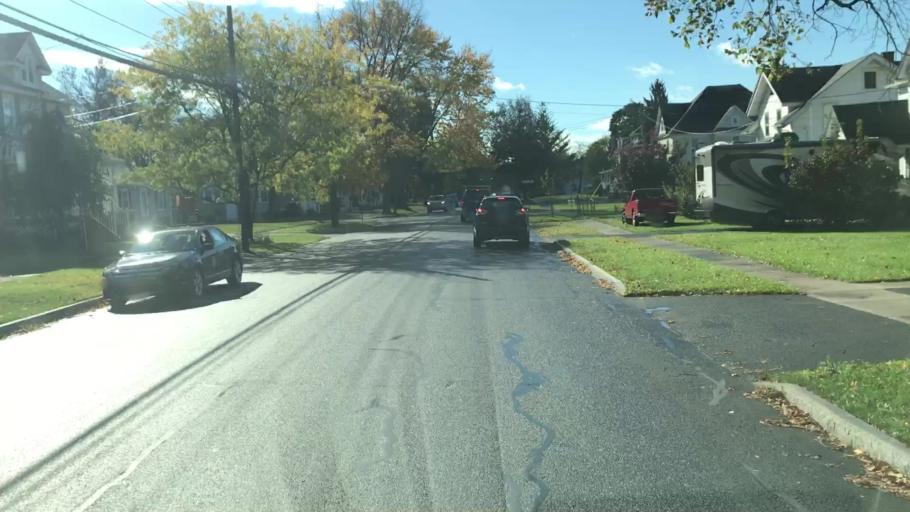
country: US
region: New York
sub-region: Cayuga County
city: Auburn
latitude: 42.9222
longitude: -76.5536
